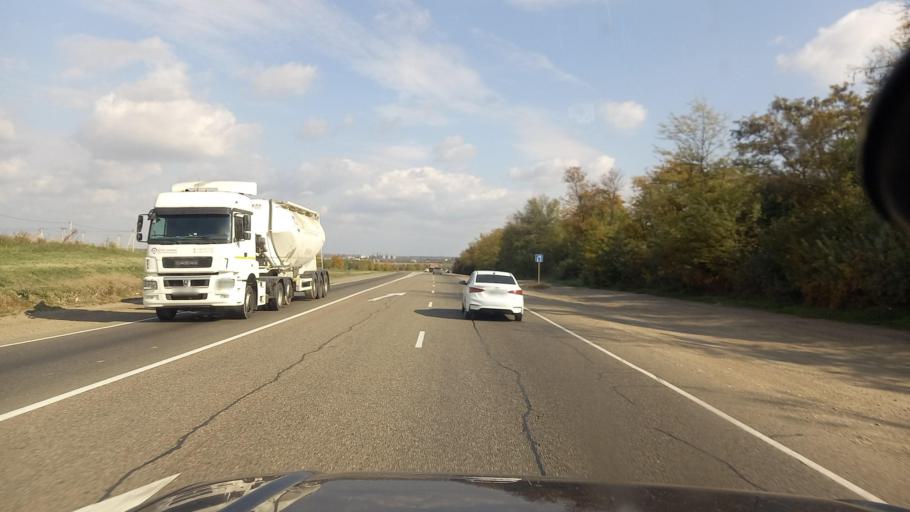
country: RU
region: Krasnodarskiy
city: Akhtyrskiy
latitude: 44.8480
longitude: 38.3142
